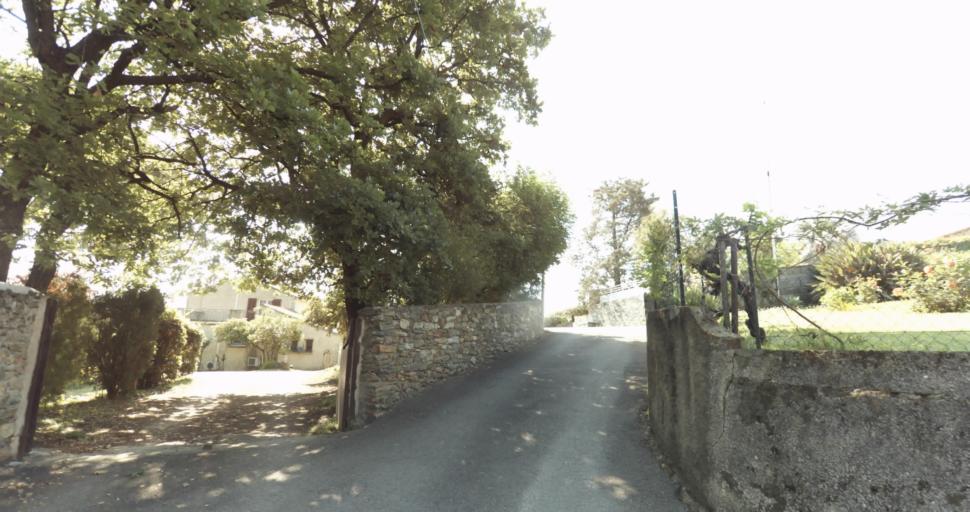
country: FR
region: Corsica
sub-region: Departement de la Haute-Corse
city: Biguglia
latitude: 42.6275
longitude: 9.4256
